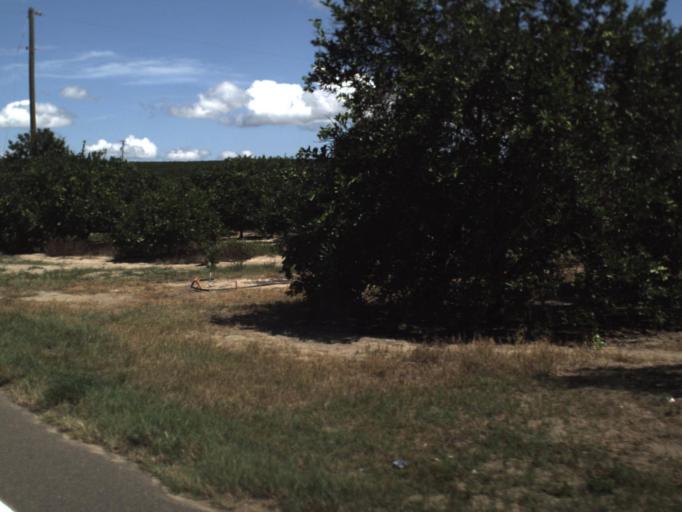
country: US
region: Florida
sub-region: Polk County
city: Babson Park
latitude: 27.7967
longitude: -81.5389
